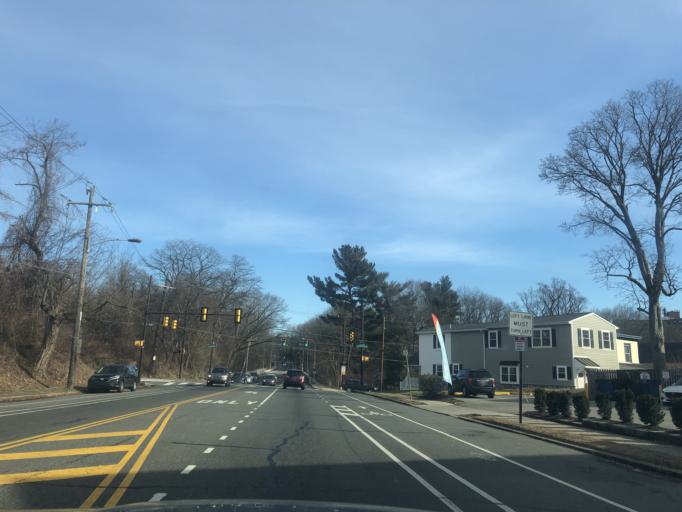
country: US
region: Pennsylvania
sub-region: Montgomery County
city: Wyndmoor
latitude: 40.0323
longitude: -75.1908
